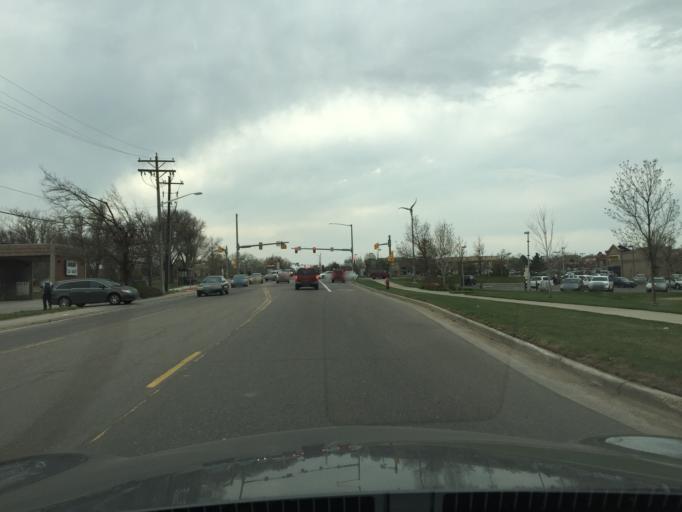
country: US
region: Colorado
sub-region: Boulder County
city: Lafayette
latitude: 40.0003
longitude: -105.0990
